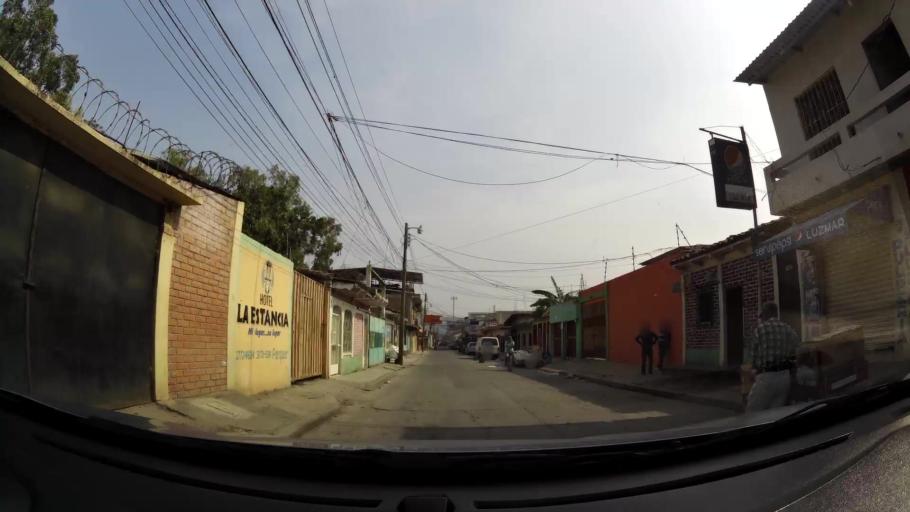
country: HN
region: Comayagua
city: Comayagua
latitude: 14.4532
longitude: -87.6420
